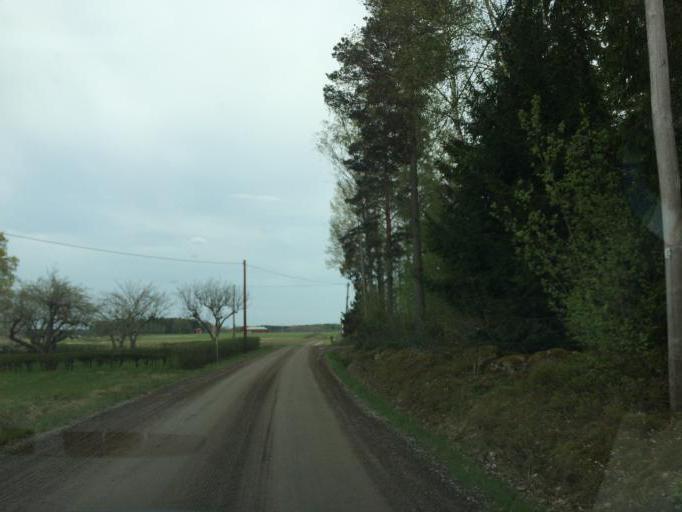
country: SE
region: Vaestmanland
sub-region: Kopings Kommun
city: Koping
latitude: 59.6108
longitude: 16.0588
